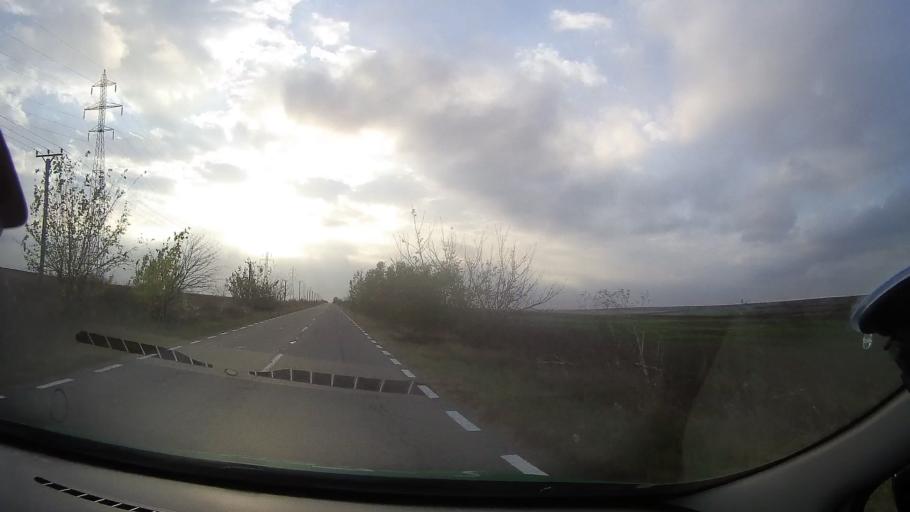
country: RO
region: Constanta
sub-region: Comuna Mircea Voda
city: Satu Nou
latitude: 44.2161
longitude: 28.1892
